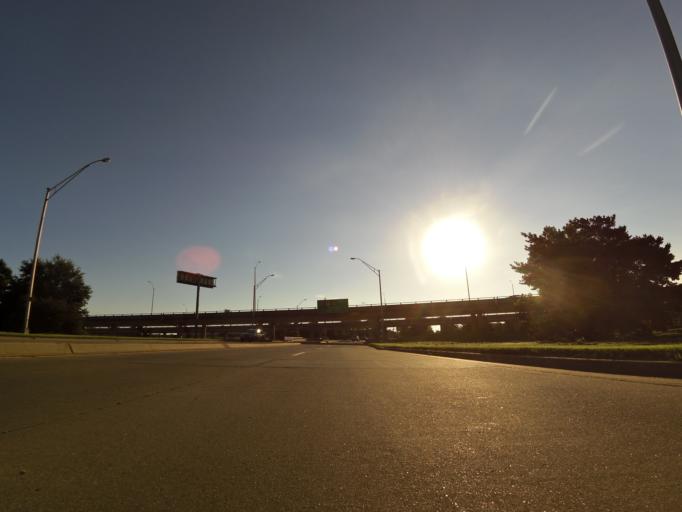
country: US
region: Kansas
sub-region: Sedgwick County
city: Wichita
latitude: 37.7000
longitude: -97.3189
